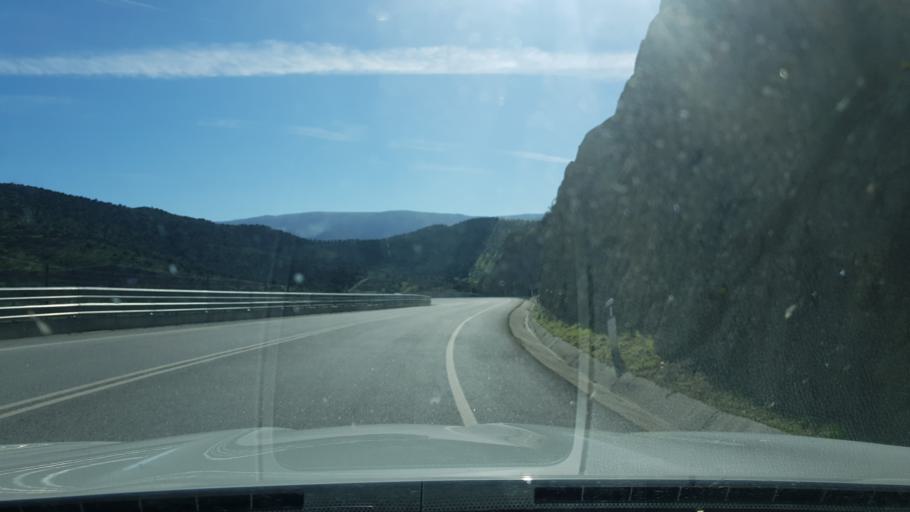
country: PT
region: Braganca
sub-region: Torre de Moncorvo
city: Torre de Moncorvo
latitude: 41.2114
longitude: -7.0860
